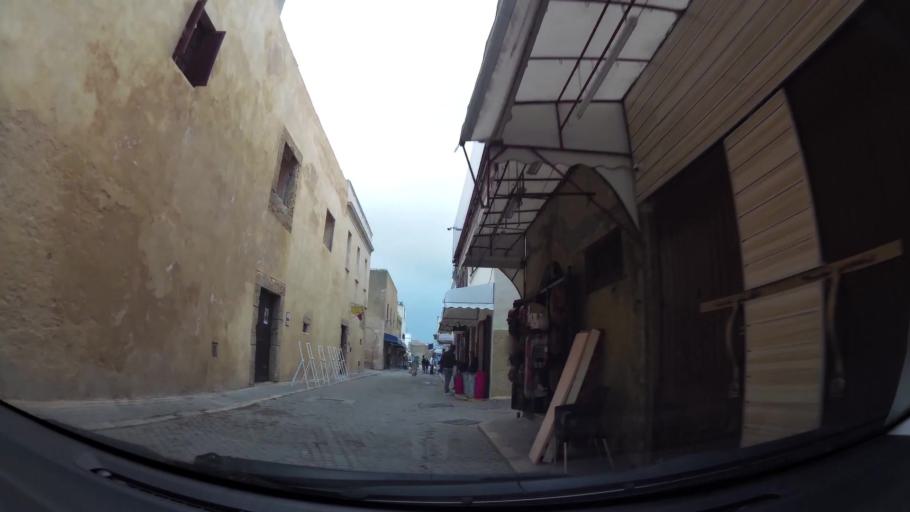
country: MA
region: Doukkala-Abda
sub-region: El-Jadida
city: El Jadida
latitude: 33.2563
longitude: -8.5027
